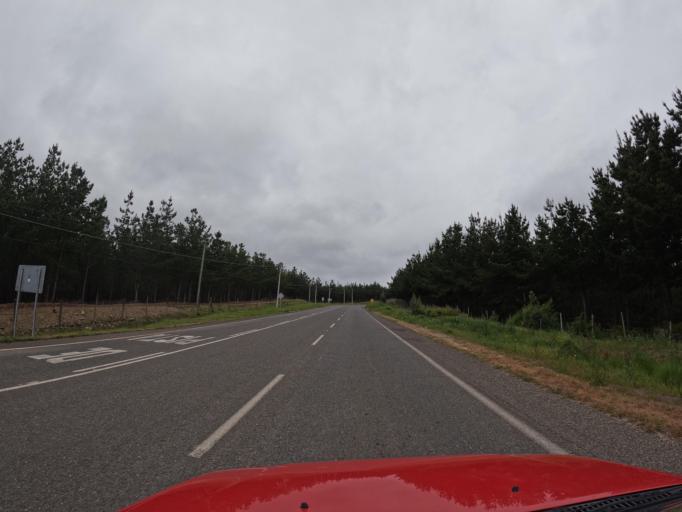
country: CL
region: O'Higgins
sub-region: Provincia de Colchagua
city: Santa Cruz
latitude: -34.6345
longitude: -72.0321
